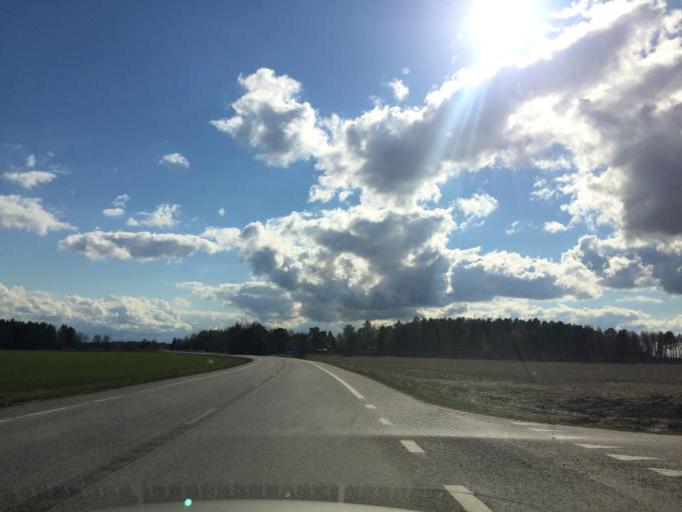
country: SE
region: Soedermanland
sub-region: Eskilstuna Kommun
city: Eskilstuna
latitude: 59.4160
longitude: 16.5884
